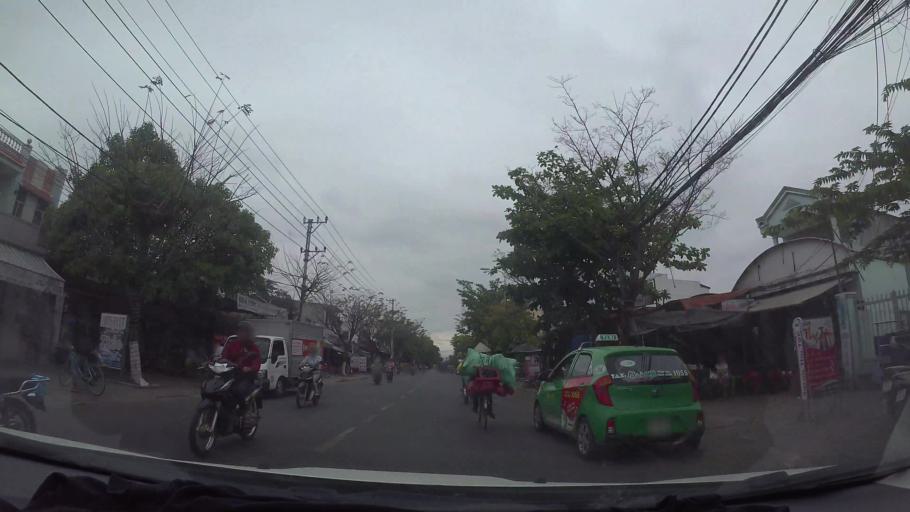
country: VN
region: Da Nang
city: Lien Chieu
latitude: 16.0699
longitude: 108.1454
